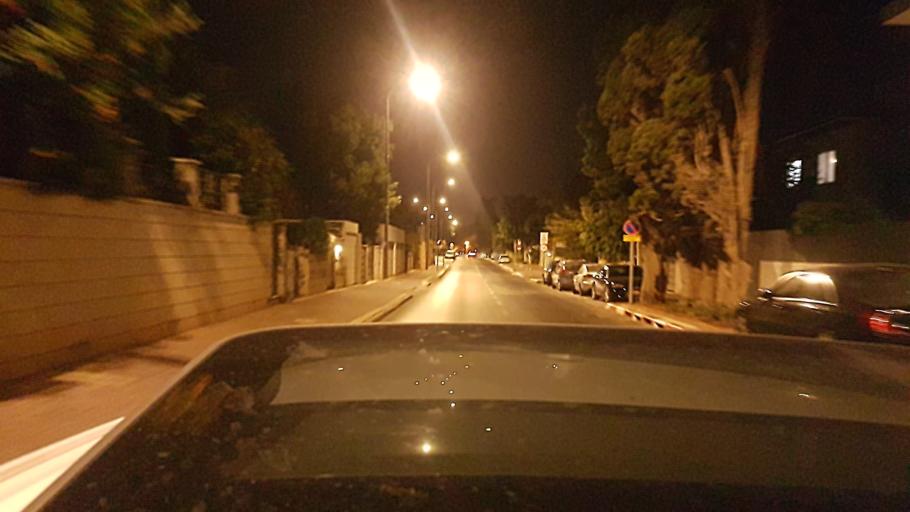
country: IL
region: Central District
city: Hod HaSharon
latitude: 32.1596
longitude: 34.8869
